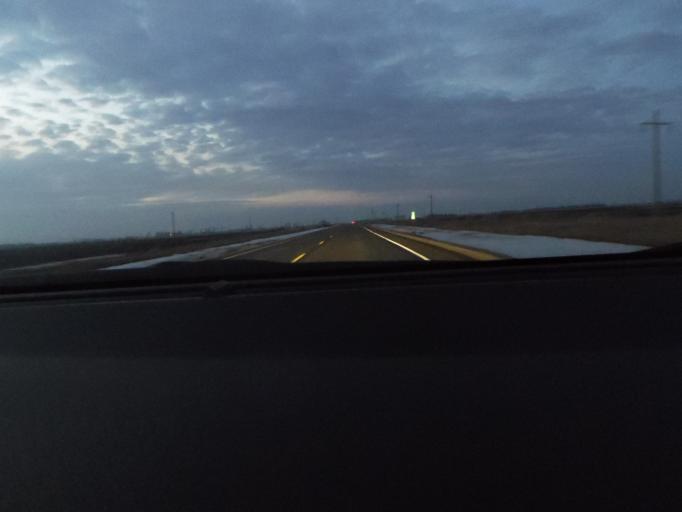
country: US
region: North Dakota
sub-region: Walsh County
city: Park River
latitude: 48.2031
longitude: -97.6227
